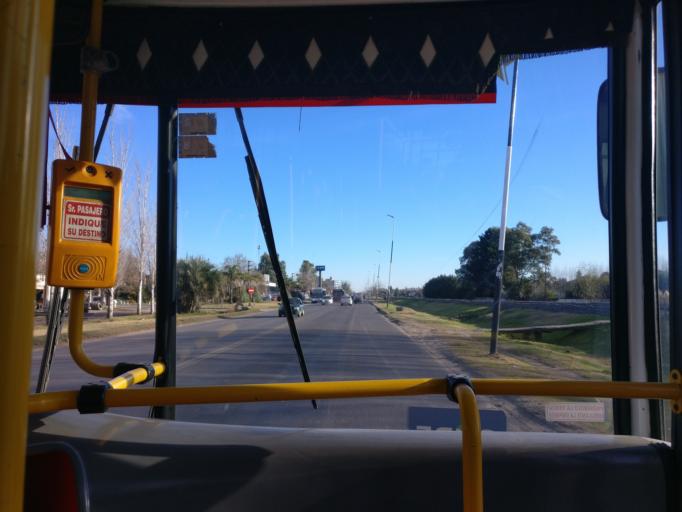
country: AR
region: Buenos Aires
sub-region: Partido de Ezeiza
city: Ezeiza
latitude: -34.8766
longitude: -58.5512
